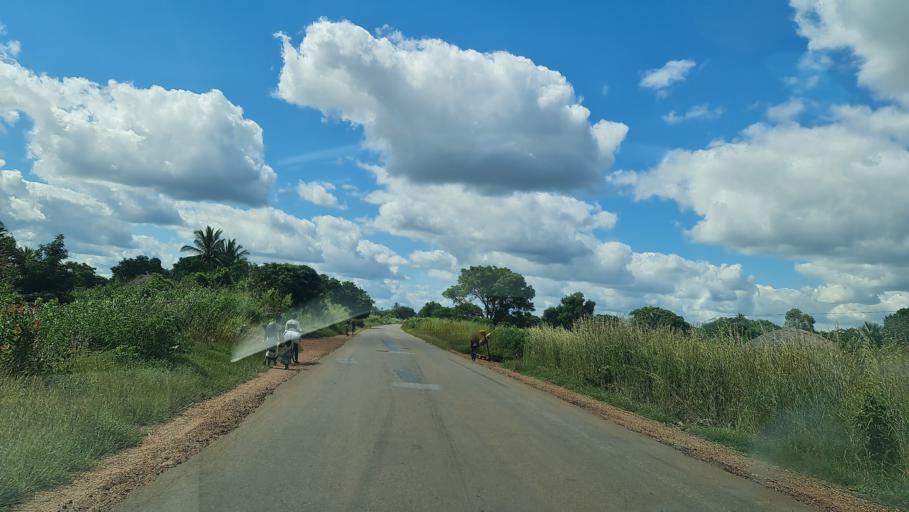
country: MZ
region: Zambezia
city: Quelimane
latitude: -17.5171
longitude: 36.2189
